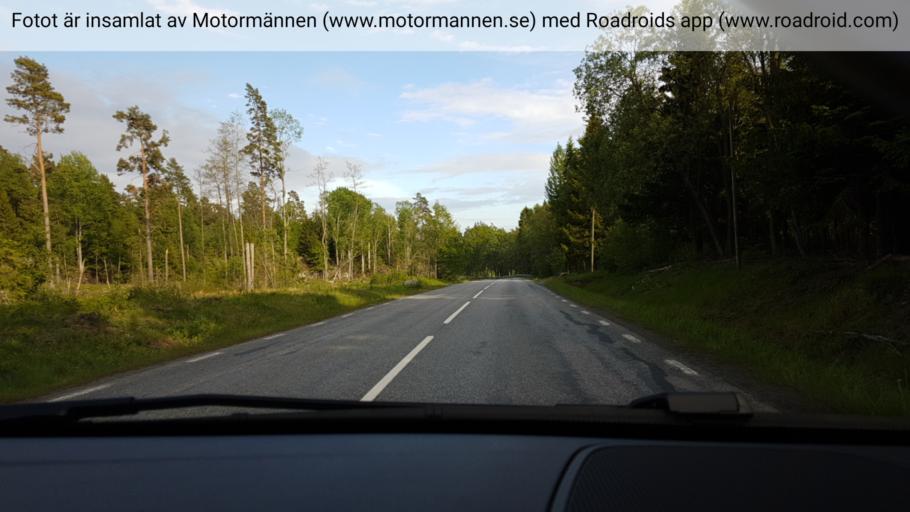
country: SE
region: Stockholm
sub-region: Nynashamns Kommun
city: Osmo
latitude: 58.9701
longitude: 17.9406
